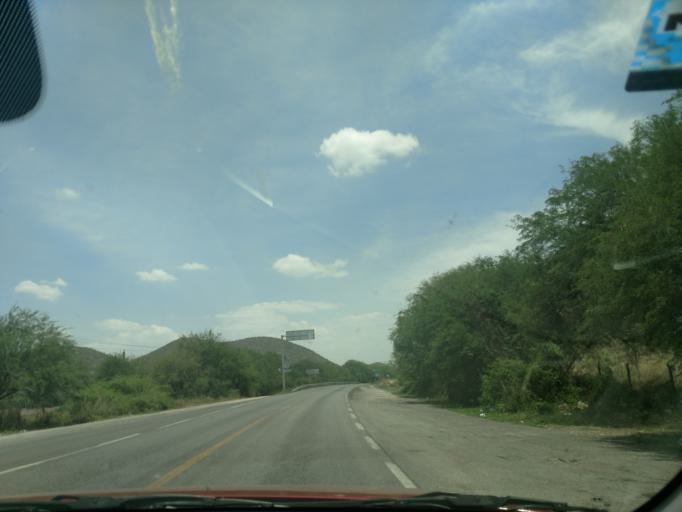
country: MX
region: San Luis Potosi
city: Ciudad Fernandez
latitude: 22.0051
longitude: -100.1471
